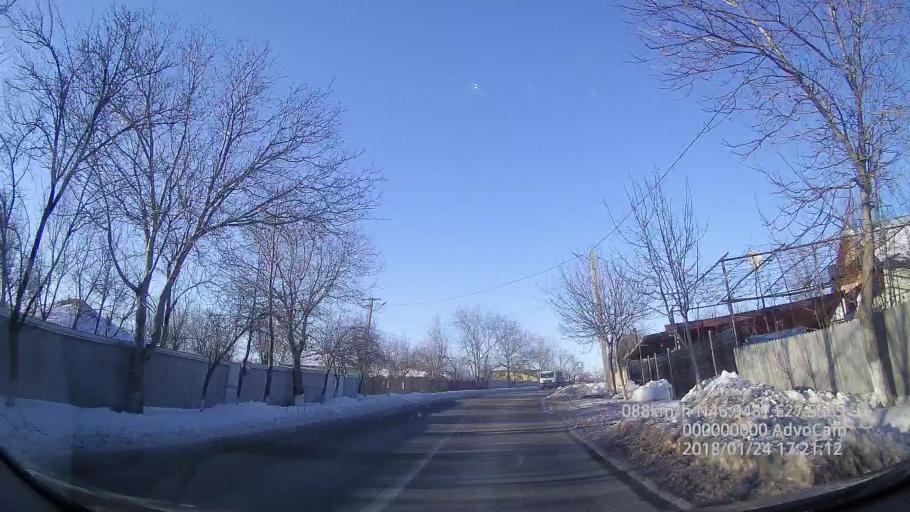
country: RO
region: Iasi
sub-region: Comuna Scanteia
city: Scanteia
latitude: 46.9493
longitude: 27.5563
